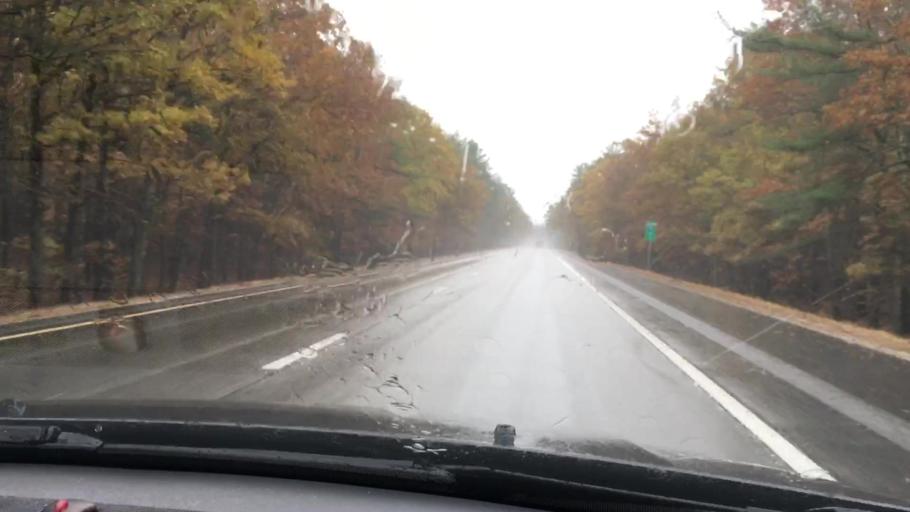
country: US
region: New Hampshire
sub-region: Merrimack County
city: Canterbury
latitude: 43.3050
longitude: -71.5839
